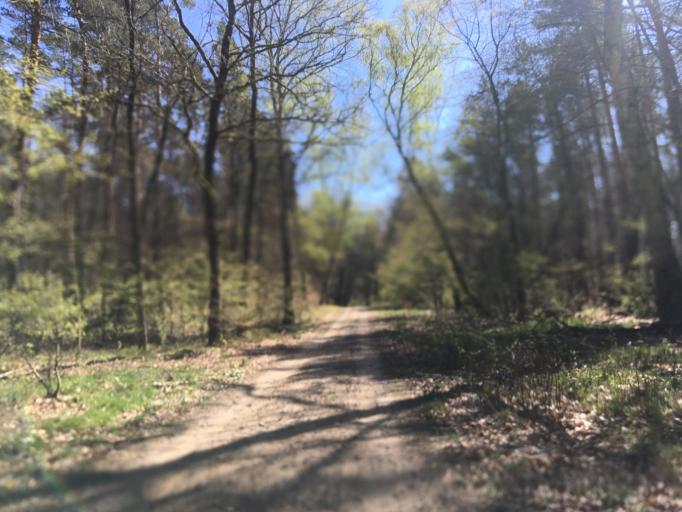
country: DE
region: Brandenburg
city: Bernau bei Berlin
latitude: 52.7005
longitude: 13.5355
